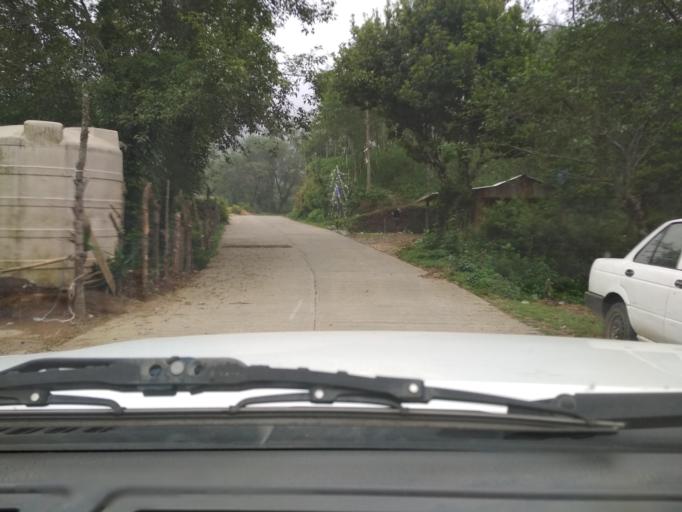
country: MX
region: Veracruz
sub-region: La Perla
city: Metlac Hernandez (Metlac Primero)
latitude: 18.9701
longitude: -97.1399
